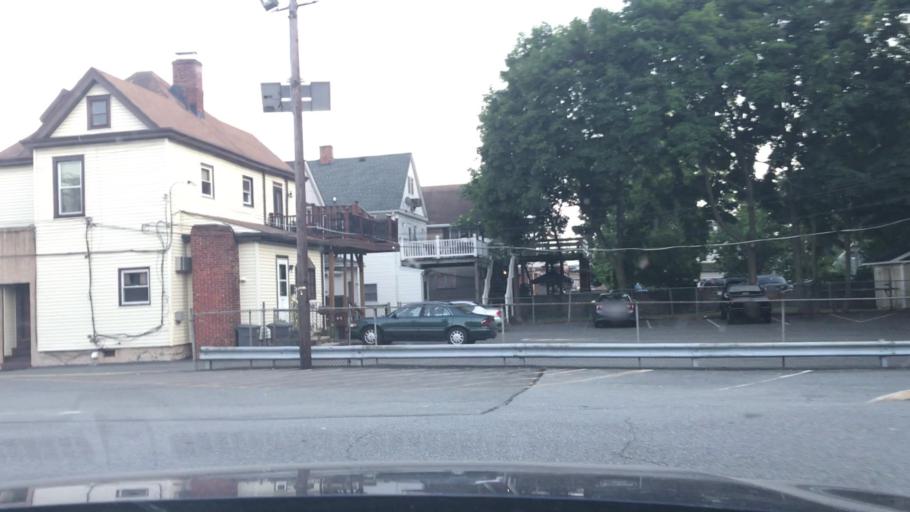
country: US
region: New Jersey
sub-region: Bergen County
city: Dumont
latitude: 40.9397
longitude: -73.9944
